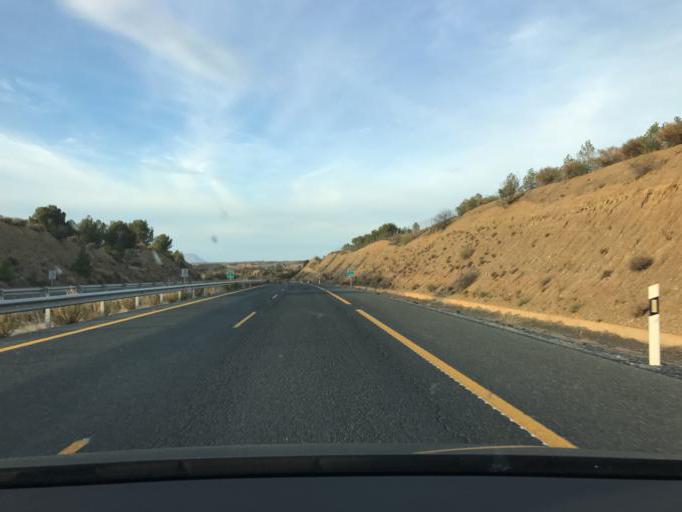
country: ES
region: Andalusia
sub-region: Provincia de Granada
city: Guadix
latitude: 37.2748
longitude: -3.0954
